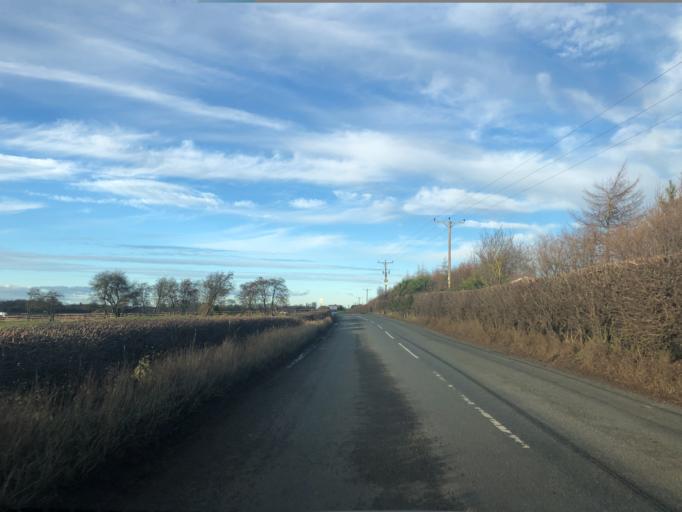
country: GB
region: England
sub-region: North Yorkshire
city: Thirsk
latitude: 54.1757
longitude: -1.3687
